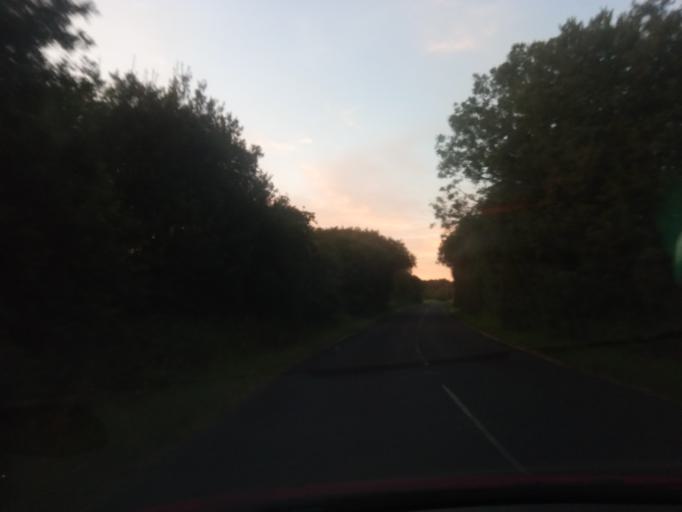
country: GB
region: England
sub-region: Northumberland
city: Bardon Mill
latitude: 54.9427
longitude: -2.2861
